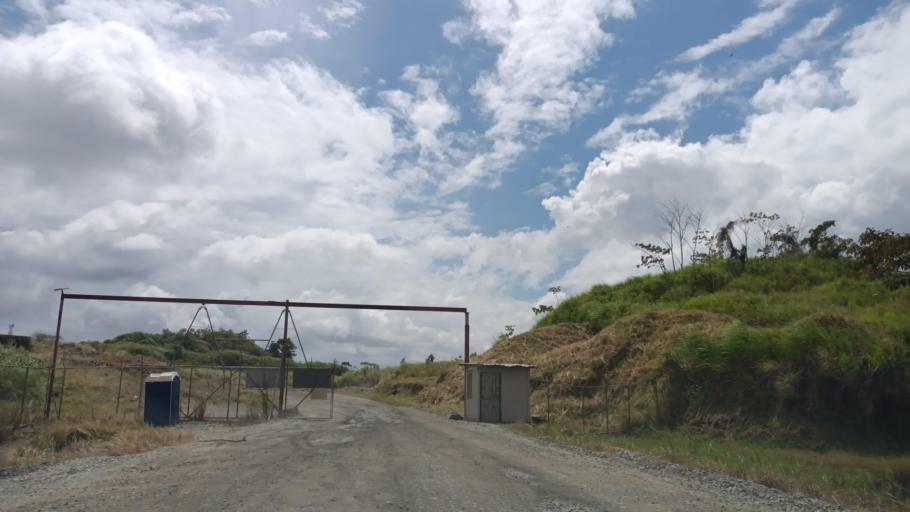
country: PA
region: Panama
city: Las Cumbres
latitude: 9.1073
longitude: -79.4999
